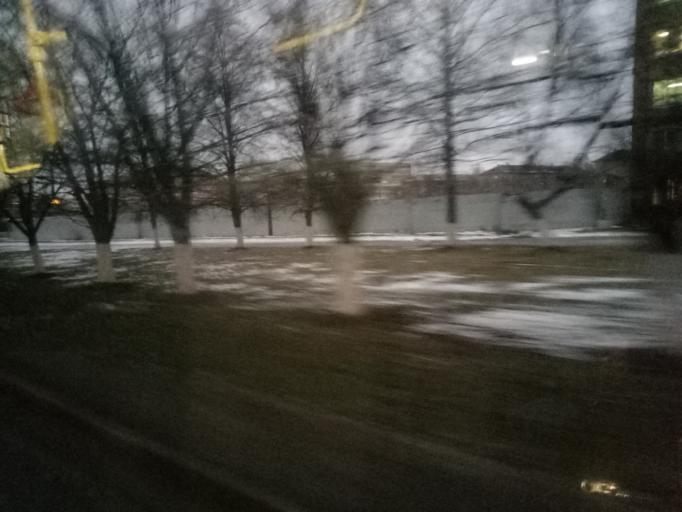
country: RU
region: Tula
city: Tula
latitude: 54.2007
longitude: 37.5854
